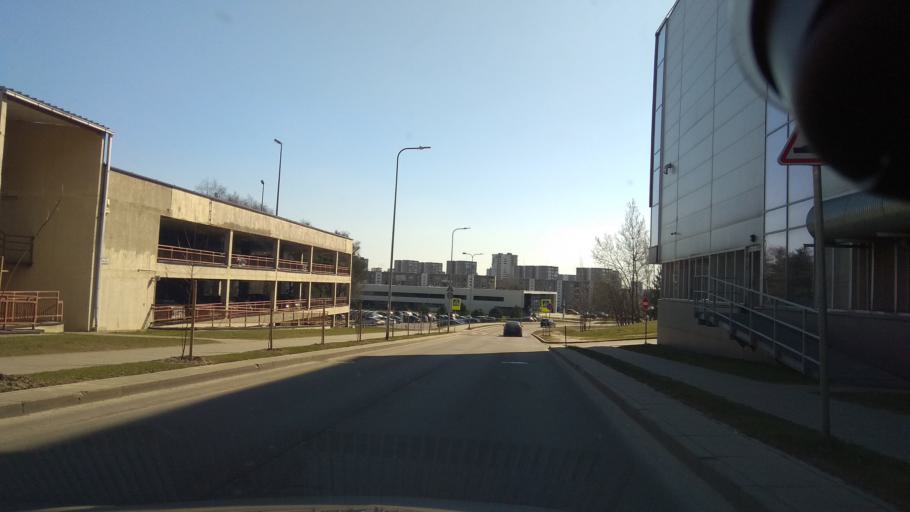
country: LT
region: Vilnius County
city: Pasilaiciai
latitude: 54.7408
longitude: 25.2298
